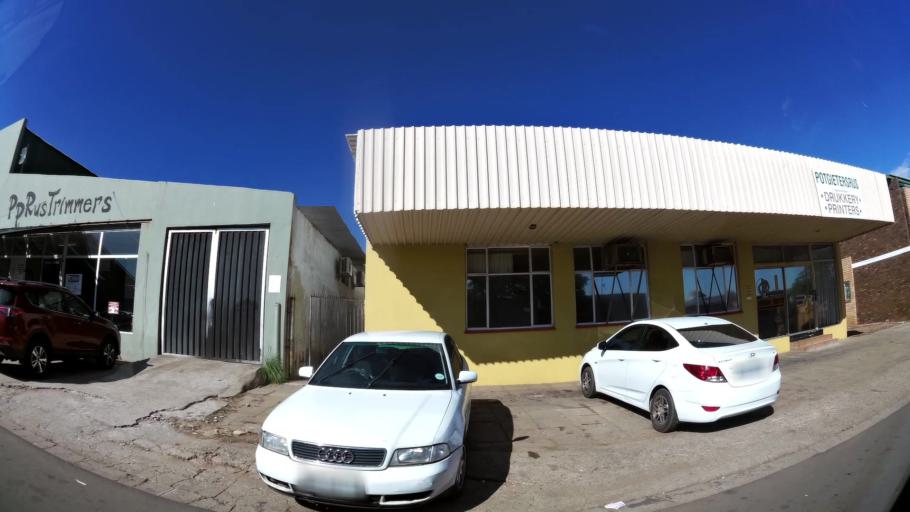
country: ZA
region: Limpopo
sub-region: Waterberg District Municipality
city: Mokopane
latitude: -24.1830
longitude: 29.0176
